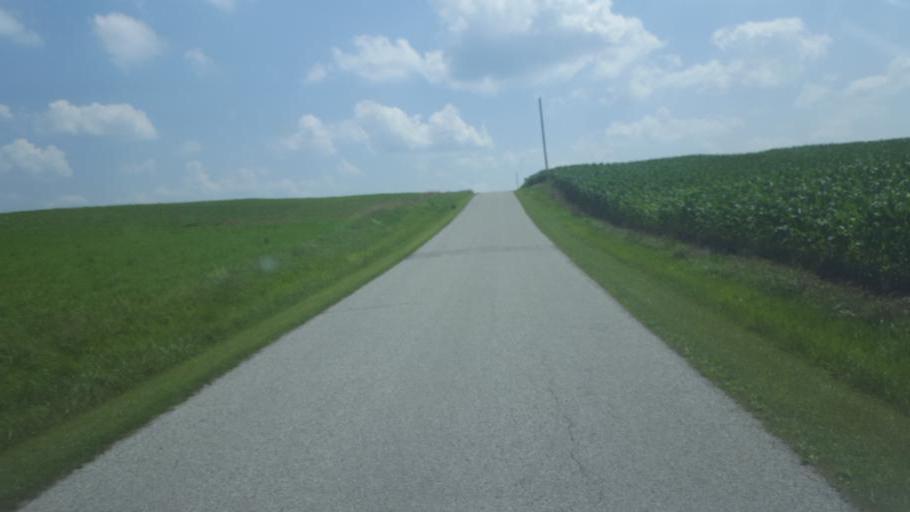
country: US
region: Ohio
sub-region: Richland County
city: Lexington
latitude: 40.6425
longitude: -82.6900
